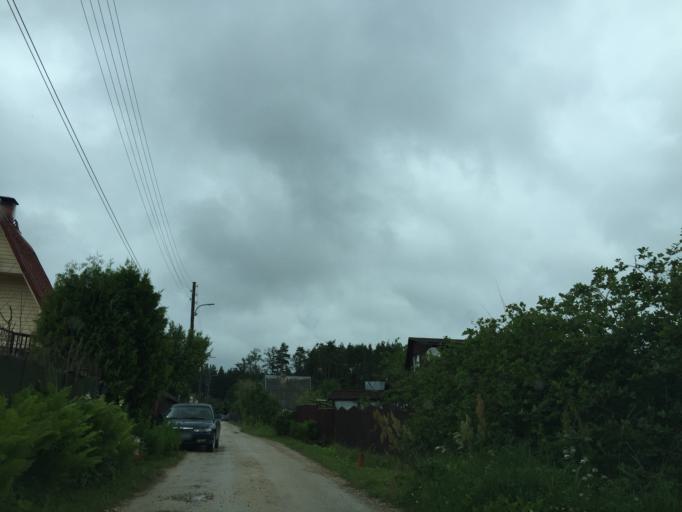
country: LV
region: Riga
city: Jaunciems
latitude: 57.0198
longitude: 24.2169
